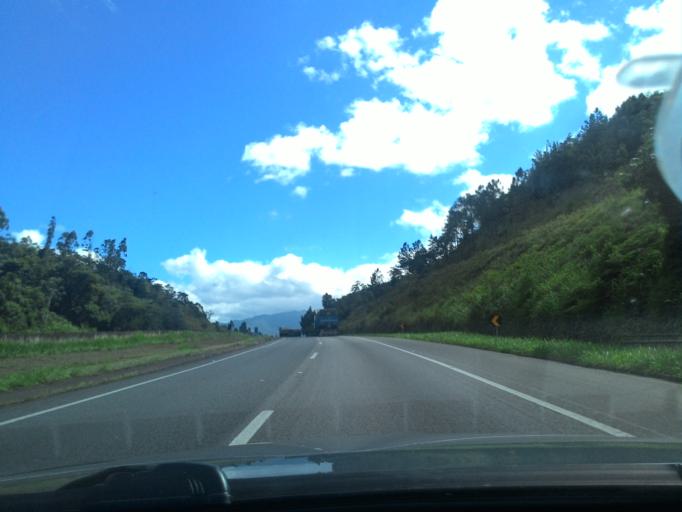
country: BR
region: Sao Paulo
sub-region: Cajati
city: Cajati
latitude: -24.7603
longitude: -48.1653
